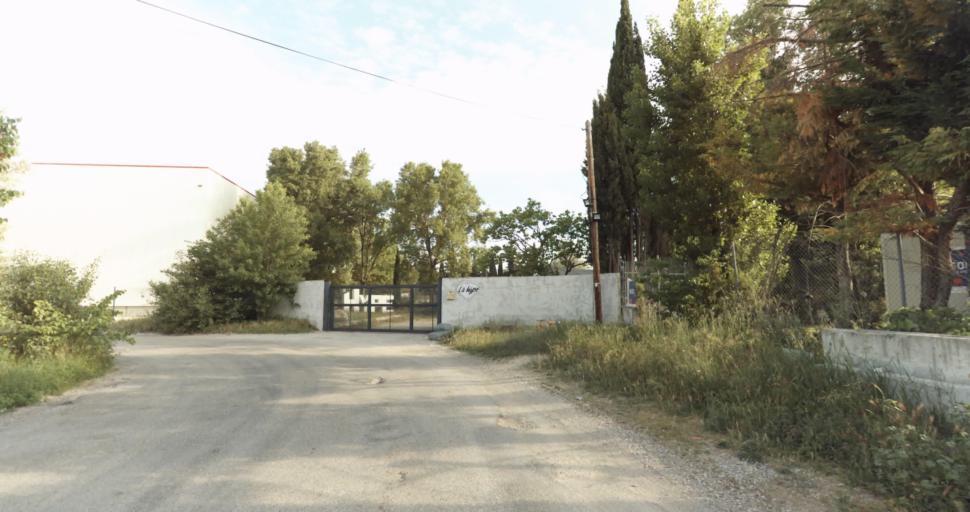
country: FR
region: Languedoc-Roussillon
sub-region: Departement du Gard
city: Rodilhan
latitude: 43.8349
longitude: 4.4213
